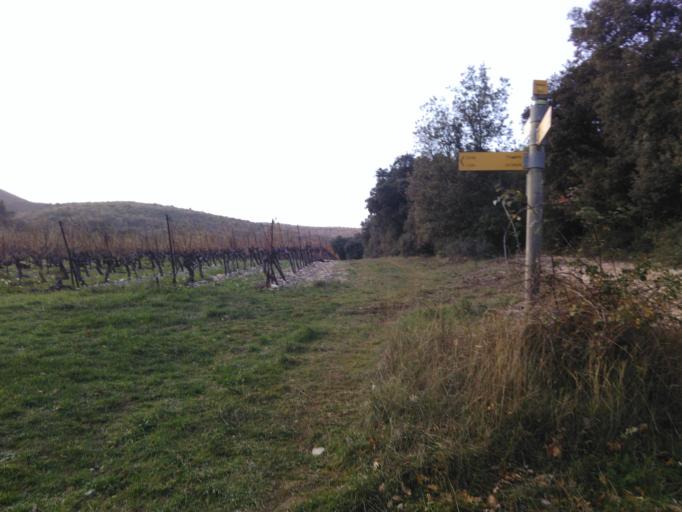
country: FR
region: Provence-Alpes-Cote d'Azur
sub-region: Departement du Vaucluse
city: Vaison-la-Romaine
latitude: 44.2139
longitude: 5.0663
